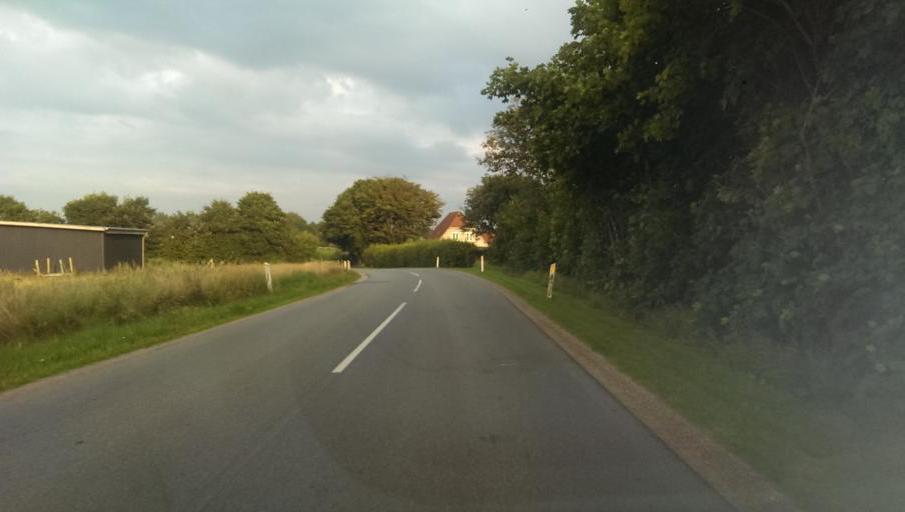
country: DK
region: South Denmark
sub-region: Esbjerg Kommune
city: Tjaereborg
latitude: 55.5586
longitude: 8.6025
